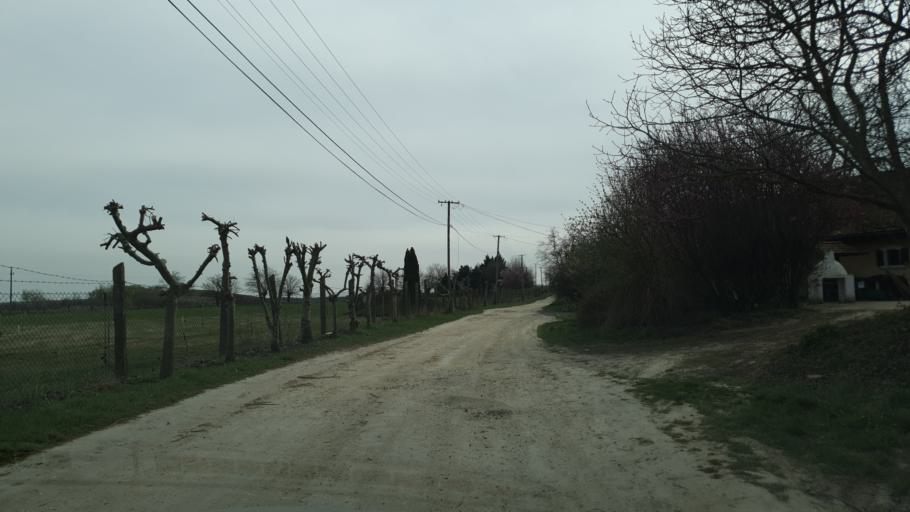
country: HU
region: Fejer
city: Etyek
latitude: 47.4380
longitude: 18.7487
